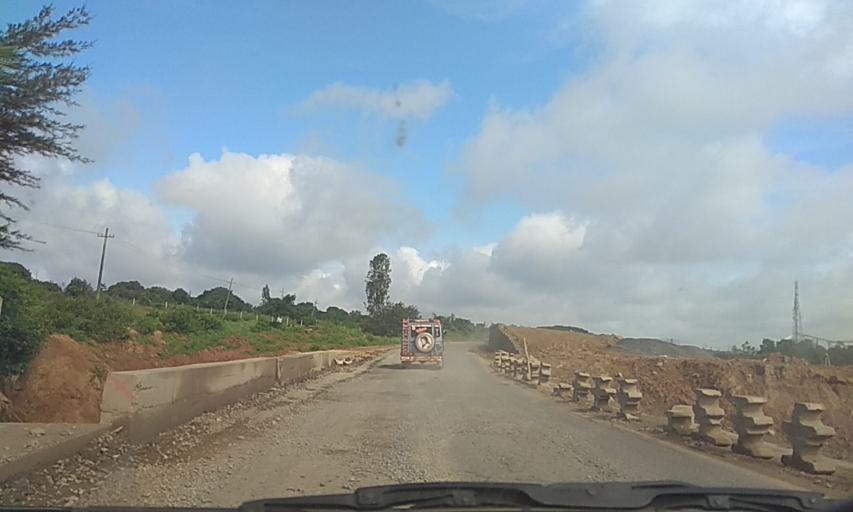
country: IN
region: Karnataka
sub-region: Haveri
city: Shiggaon
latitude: 15.0358
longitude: 75.1744
